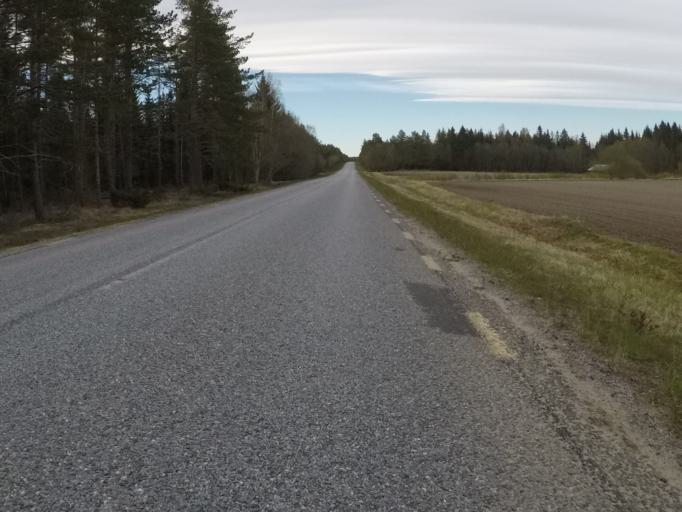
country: SE
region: Vaesterbotten
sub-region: Umea Kommun
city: Saevar
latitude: 63.9408
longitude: 20.7873
